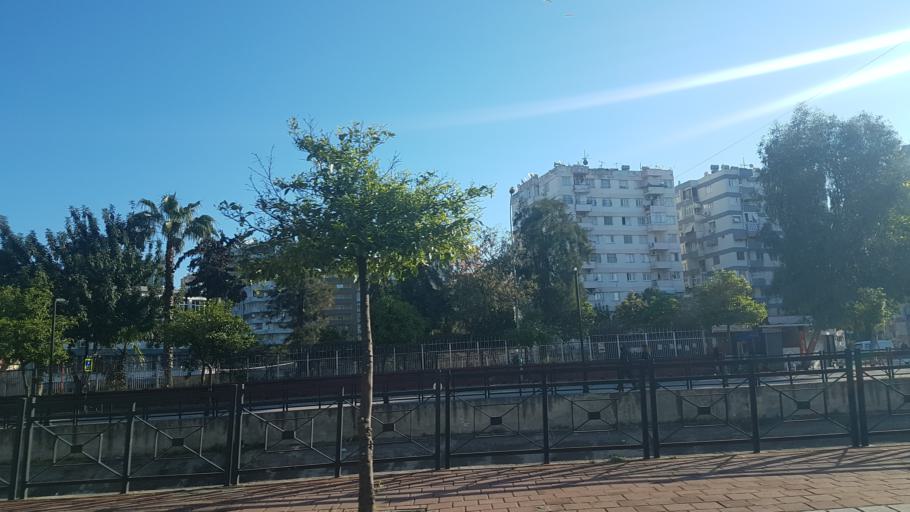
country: TR
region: Adana
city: Adana
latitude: 37.0295
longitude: 35.3098
